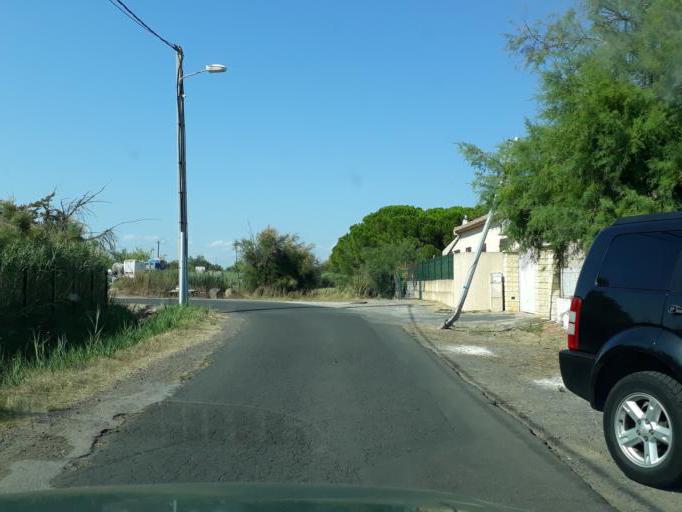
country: FR
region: Languedoc-Roussillon
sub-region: Departement de l'Herault
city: Agde
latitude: 43.2921
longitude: 3.4487
